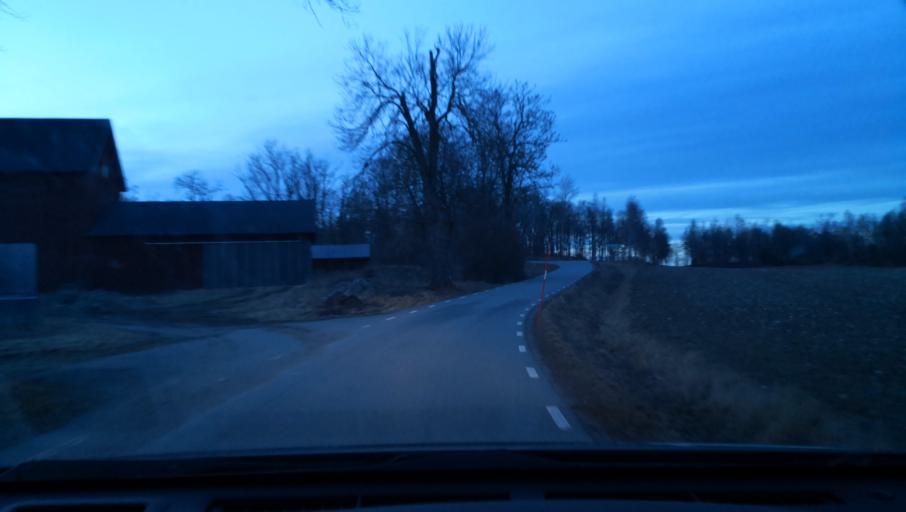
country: SE
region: Uppsala
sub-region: Enkopings Kommun
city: Dalby
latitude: 59.5490
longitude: 17.3691
